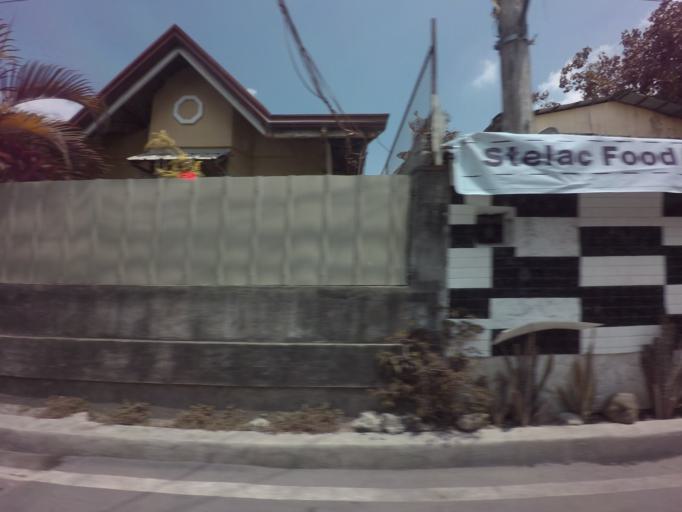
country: PH
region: Calabarzon
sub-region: Province of Laguna
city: San Pedro
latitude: 14.4022
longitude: 121.0504
